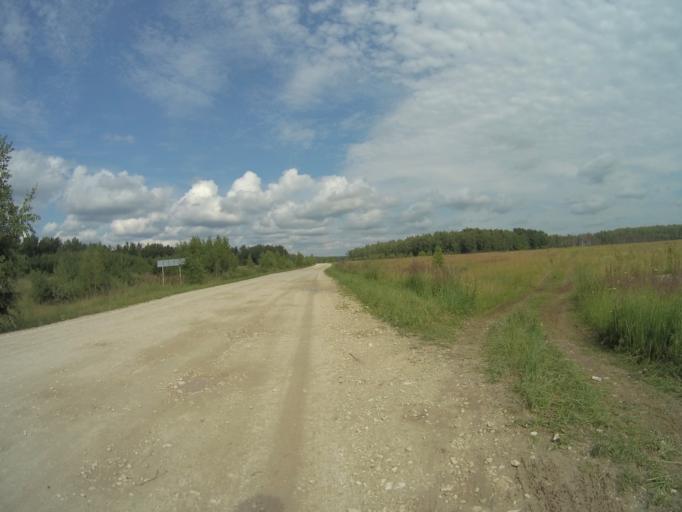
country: RU
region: Vladimir
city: Orgtrud
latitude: 56.2432
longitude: 40.6866
